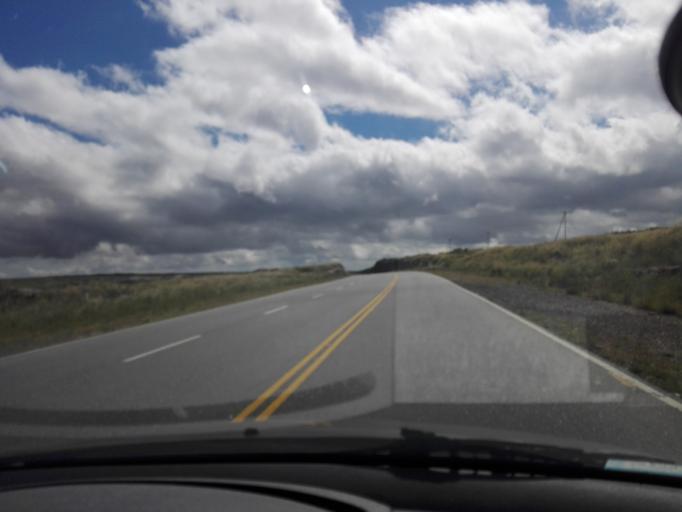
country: AR
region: Cordoba
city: Mina Clavero
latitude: -31.6106
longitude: -64.8374
